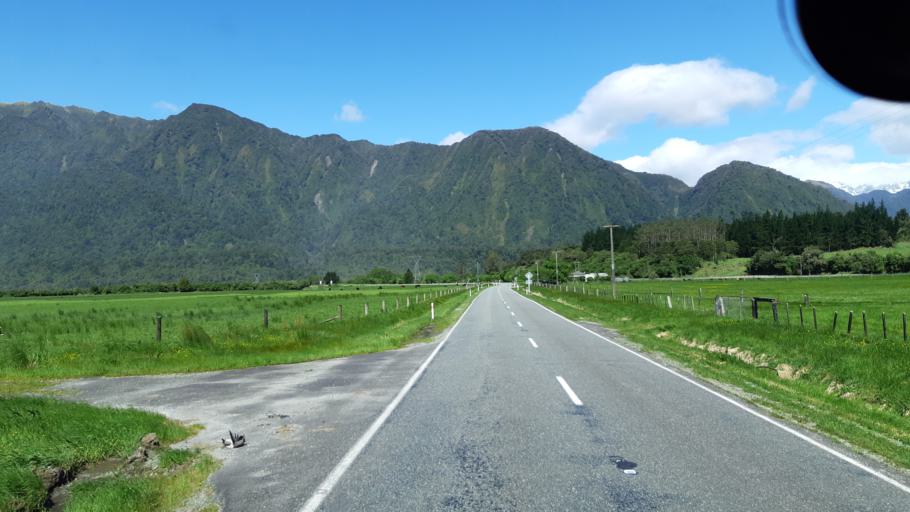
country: NZ
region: West Coast
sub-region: Westland District
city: Hokitika
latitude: -43.1535
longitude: 170.6114
